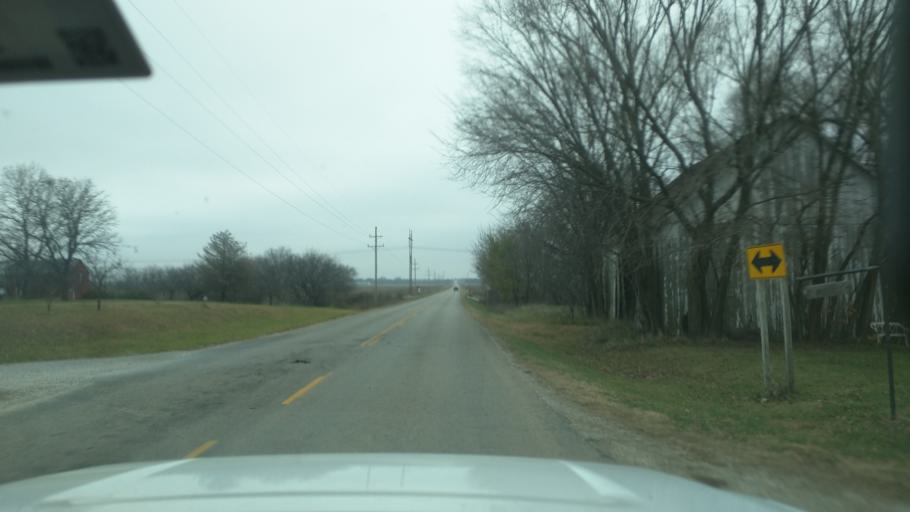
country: US
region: Kansas
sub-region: Lyon County
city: Emporia
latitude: 38.4923
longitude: -96.2528
